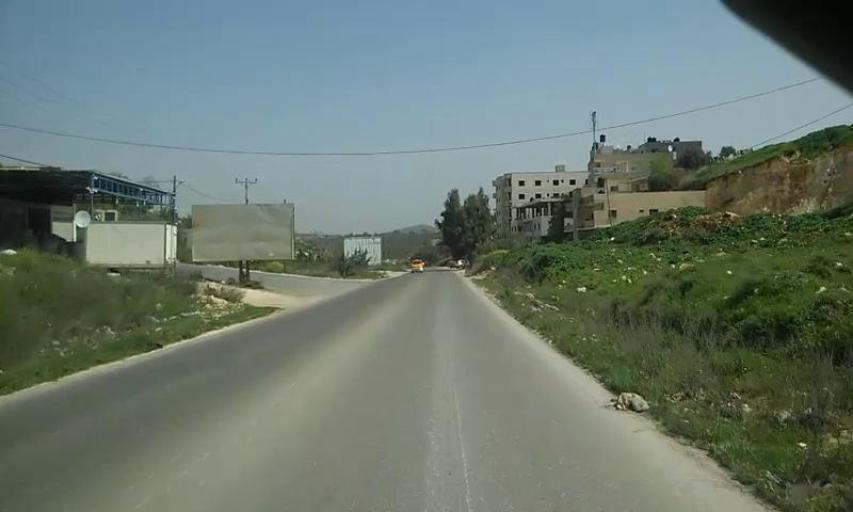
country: PS
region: West Bank
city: Ash Shuhada'
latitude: 32.4386
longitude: 35.2771
